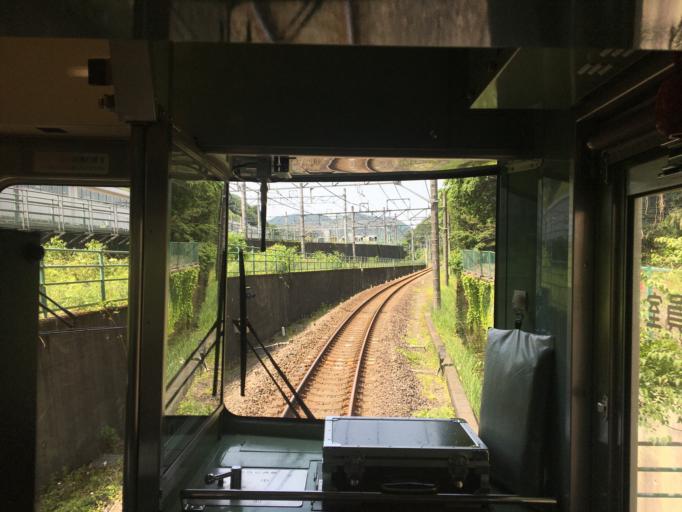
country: JP
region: Saitama
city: Hanno
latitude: 35.8700
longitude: 139.3088
